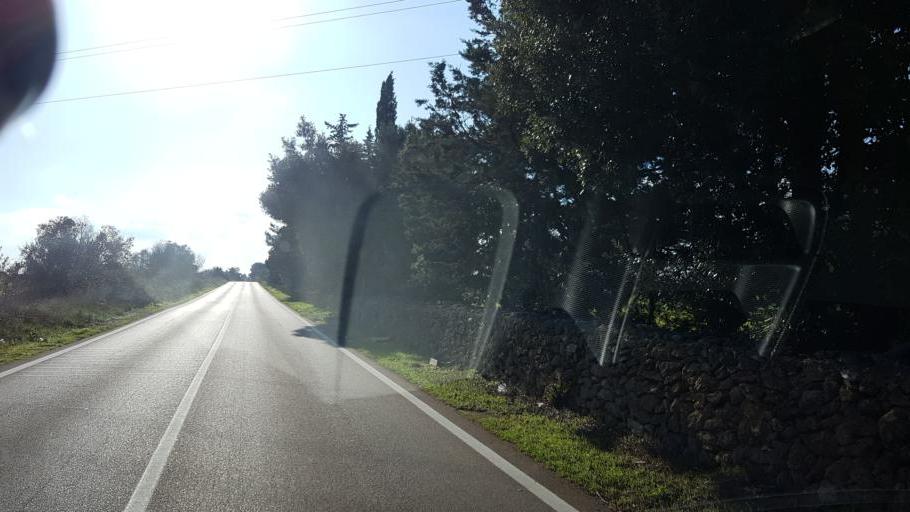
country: IT
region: Apulia
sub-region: Provincia di Lecce
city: Trepuzzi
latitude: 40.4578
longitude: 18.1140
